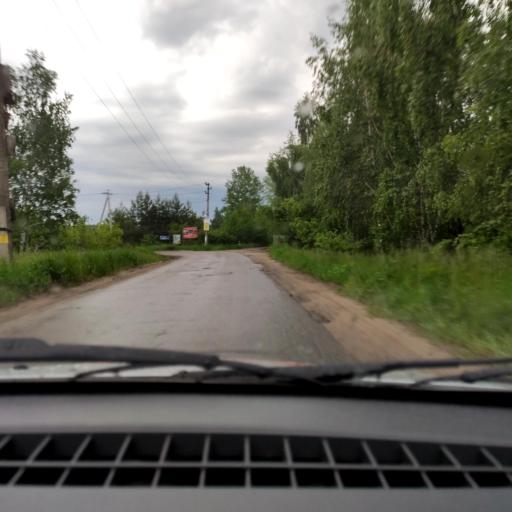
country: RU
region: Voronezj
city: Ramon'
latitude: 51.8477
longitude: 39.2330
